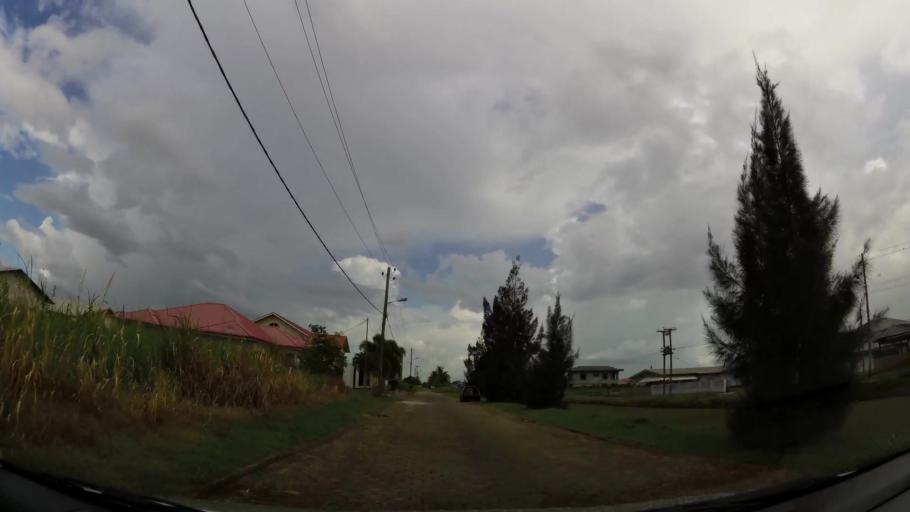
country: SR
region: Commewijne
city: Nieuw Amsterdam
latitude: 5.8626
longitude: -55.1213
